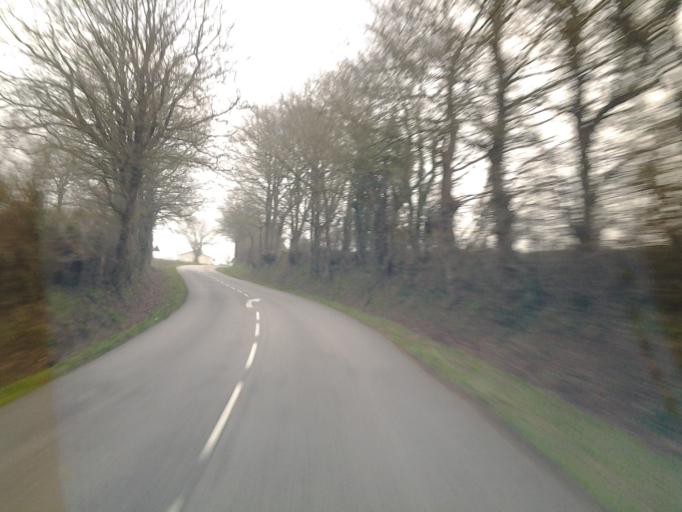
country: FR
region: Pays de la Loire
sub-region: Departement de la Vendee
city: Nesmy
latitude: 46.6219
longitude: -1.4079
